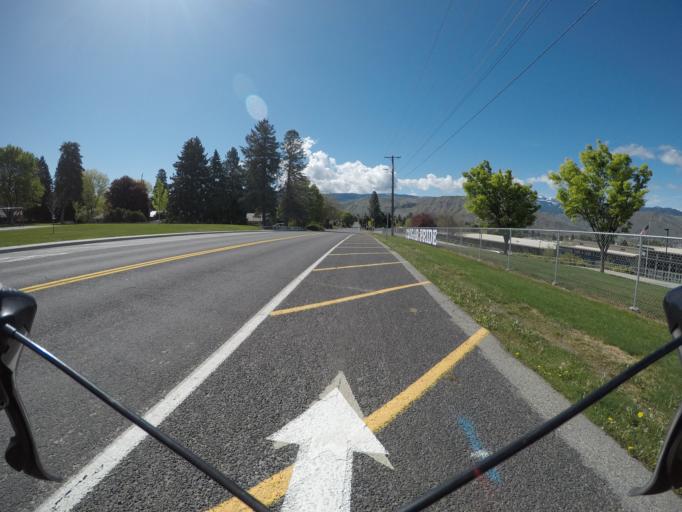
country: US
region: Washington
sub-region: Douglas County
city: East Wenatchee Bench
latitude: 47.4149
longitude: -120.2693
